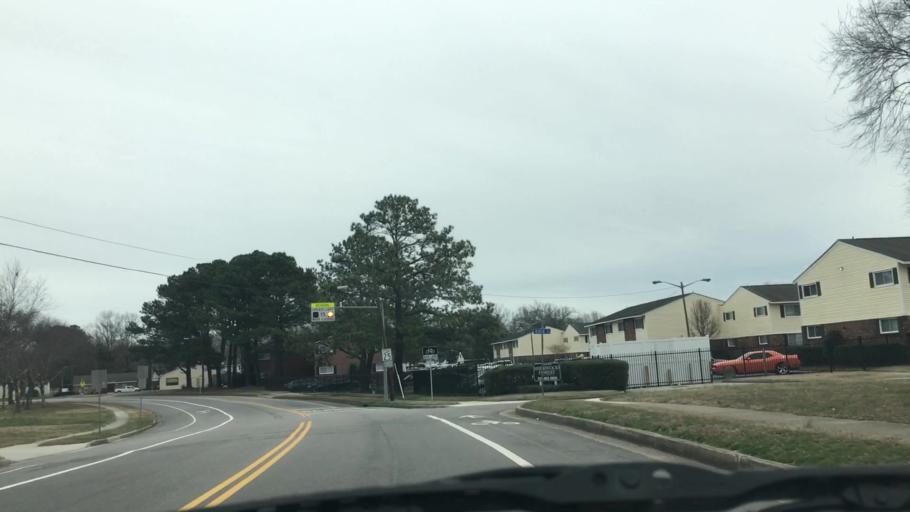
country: US
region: Virginia
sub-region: City of Norfolk
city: Norfolk
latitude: 36.8757
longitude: -76.2396
